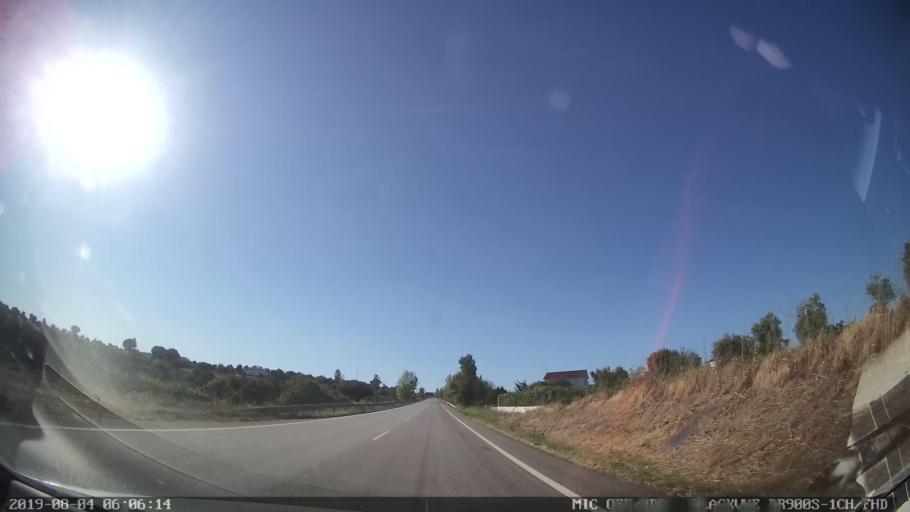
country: PT
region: Santarem
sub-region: Abrantes
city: Alferrarede
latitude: 39.4792
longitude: -8.0854
